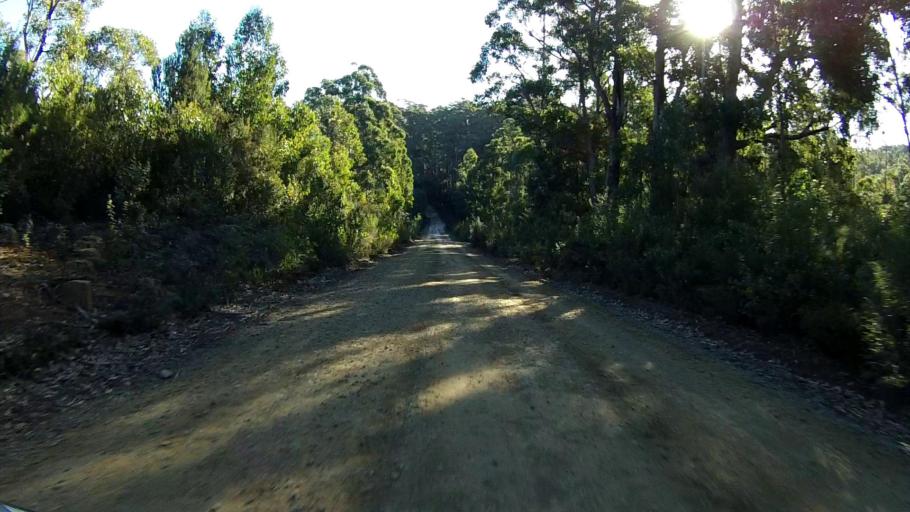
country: AU
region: Tasmania
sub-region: Clarence
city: Sandford
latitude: -43.1156
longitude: 147.9103
